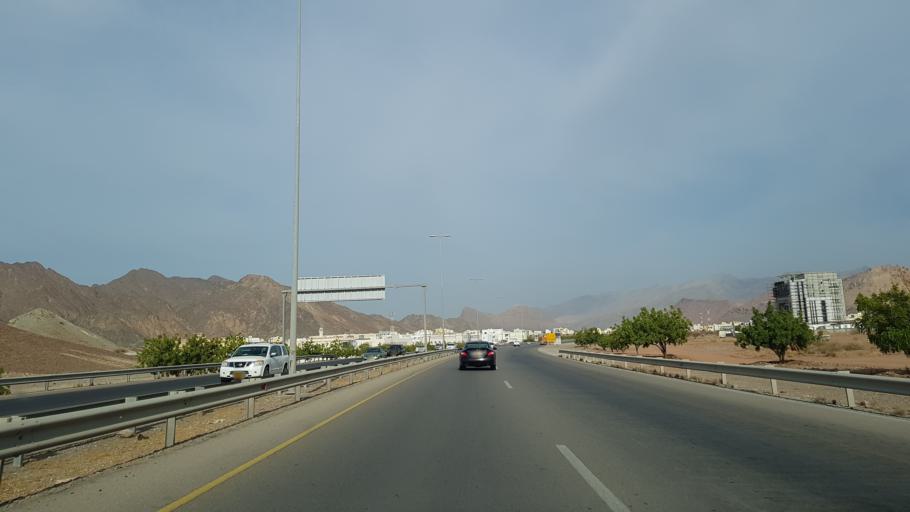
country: OM
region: Muhafazat ad Dakhiliyah
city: Bidbid
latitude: 23.4675
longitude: 58.1415
